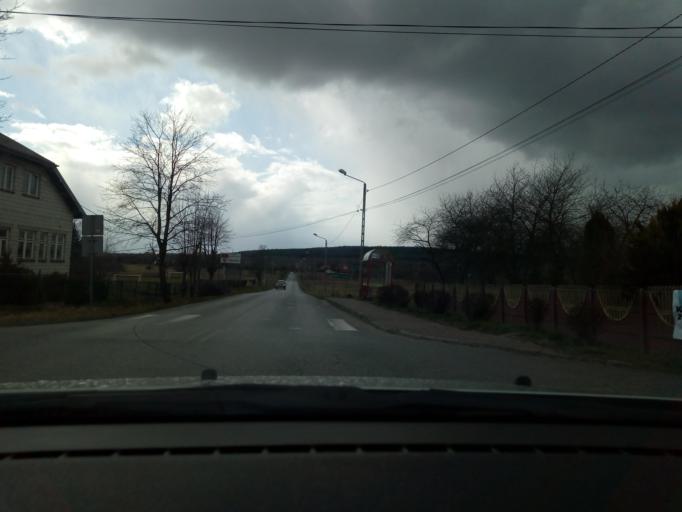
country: PL
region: Swietokrzyskie
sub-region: Powiat skarzyski
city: Skarzysko Koscielne
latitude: 51.1471
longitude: 20.8892
